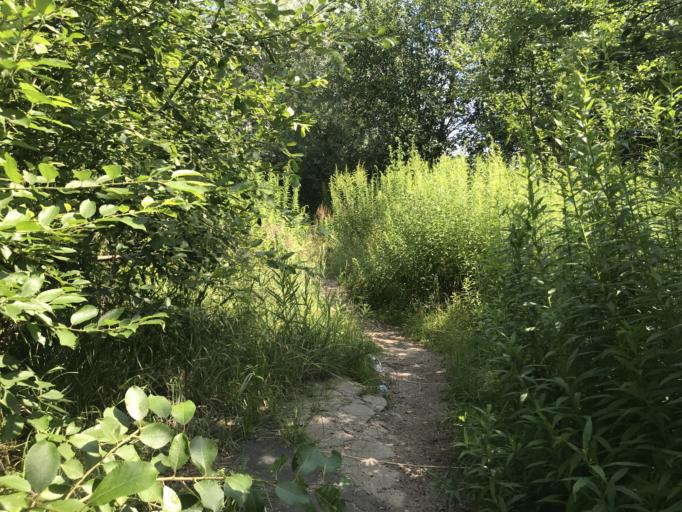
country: PL
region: Pomeranian Voivodeship
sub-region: Gdansk
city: Gdansk
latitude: 54.3438
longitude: 18.6666
